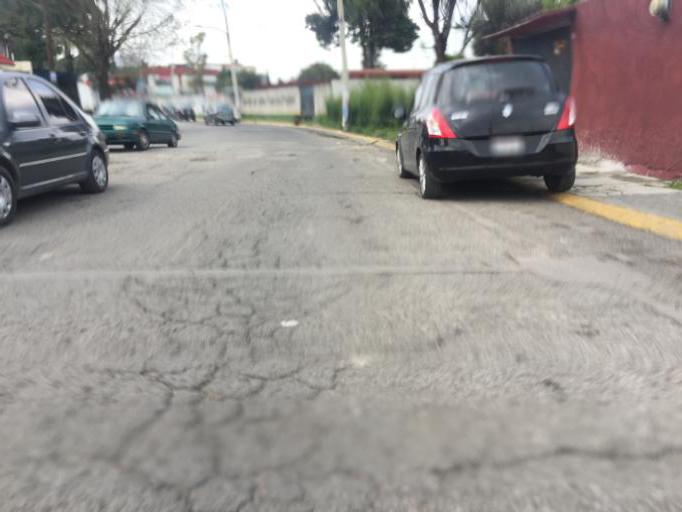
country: MX
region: Mexico
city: Cuautitlan Izcalli
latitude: 19.6582
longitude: -99.2143
